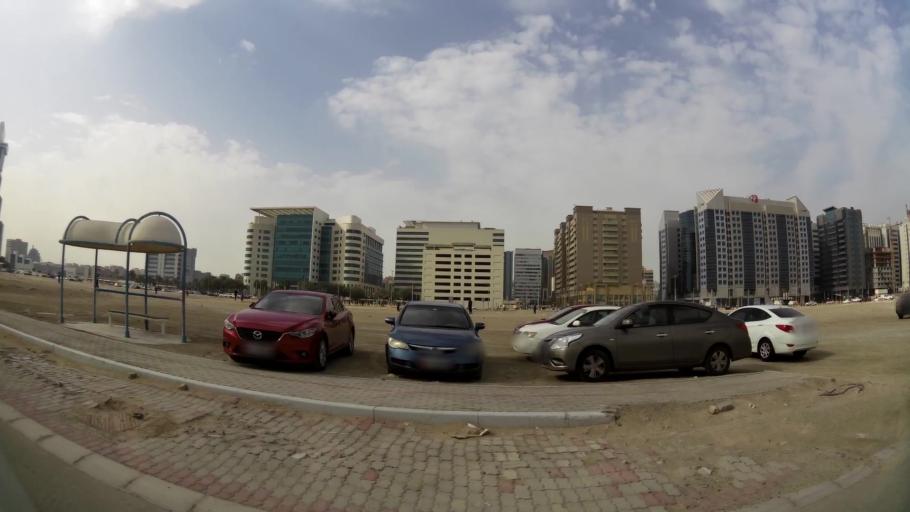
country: AE
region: Abu Dhabi
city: Abu Dhabi
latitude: 24.4656
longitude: 54.3896
